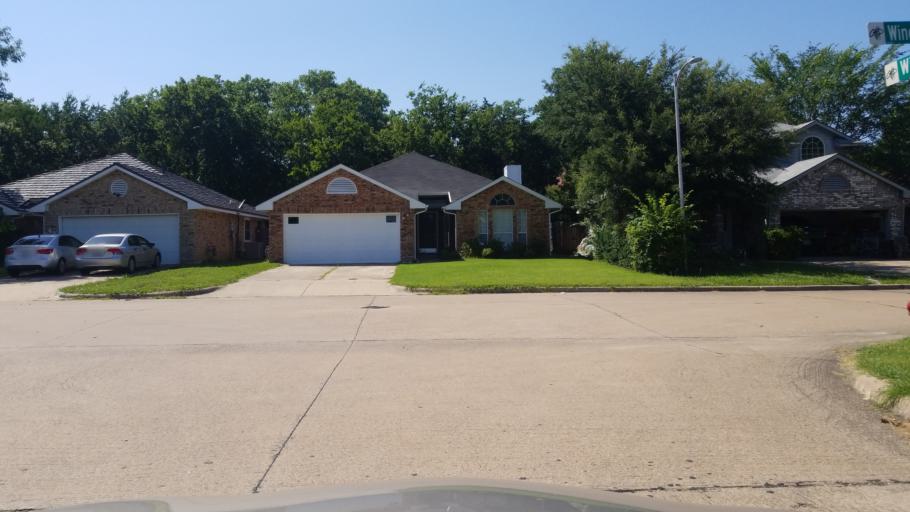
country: US
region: Texas
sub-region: Dallas County
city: Grand Prairie
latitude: 32.6915
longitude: -97.0111
